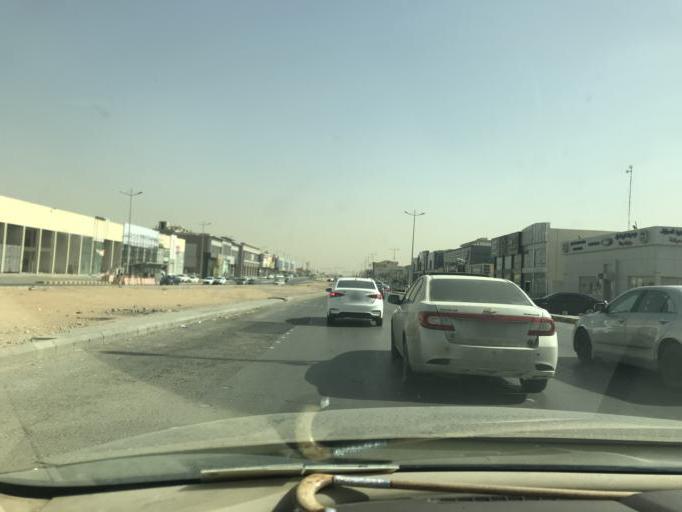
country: SA
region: Ar Riyad
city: Riyadh
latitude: 24.8049
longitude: 46.7378
